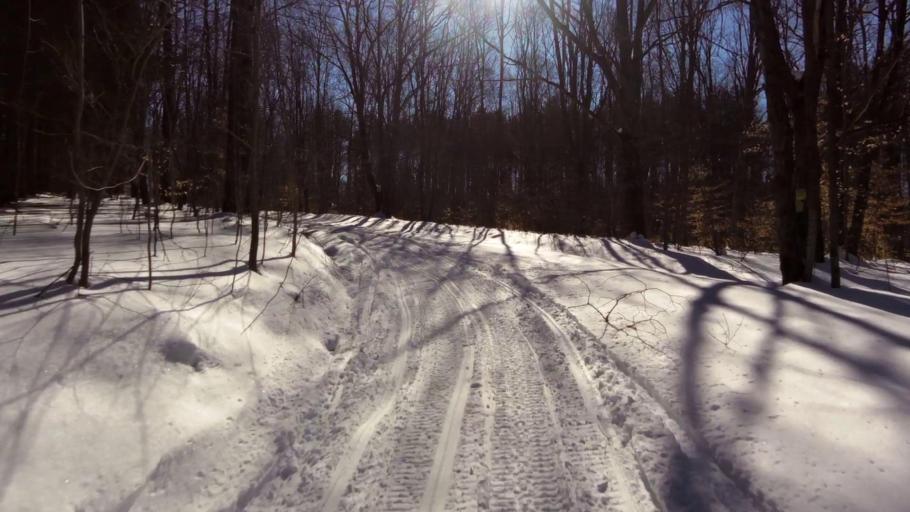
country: US
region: New York
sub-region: Allegany County
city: Cuba
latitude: 42.3053
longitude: -78.2712
